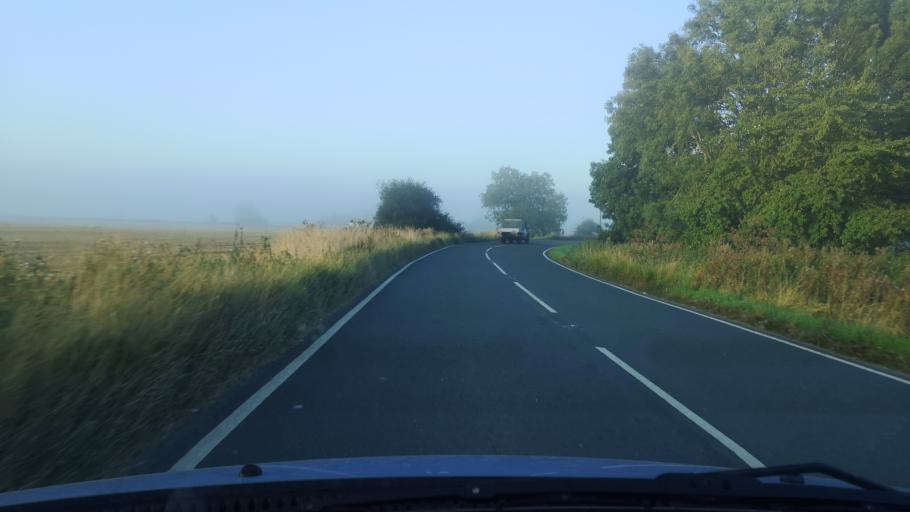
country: GB
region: England
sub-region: North Lincolnshire
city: Eastoft
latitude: 53.6585
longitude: -0.7735
